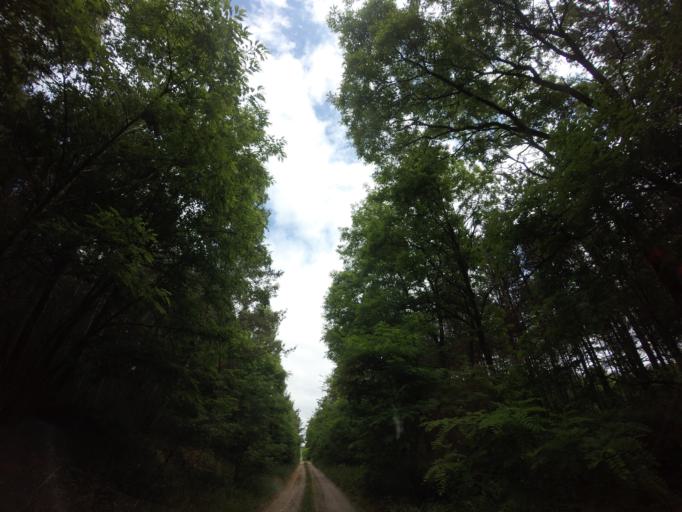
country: PL
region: West Pomeranian Voivodeship
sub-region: Powiat choszczenski
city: Krzecin
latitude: 53.0092
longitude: 15.5213
